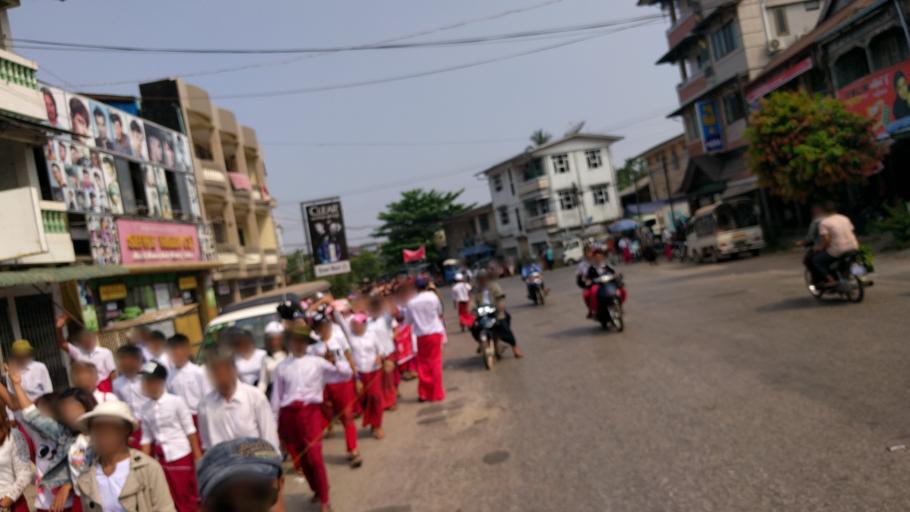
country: MM
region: Mon
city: Mawlamyine
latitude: 16.4738
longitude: 97.6220
